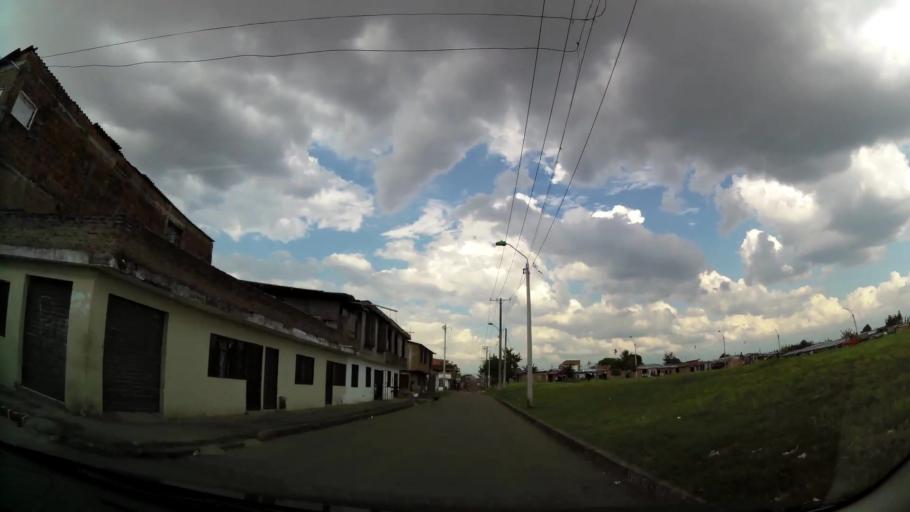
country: CO
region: Valle del Cauca
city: Cali
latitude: 3.4054
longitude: -76.4964
